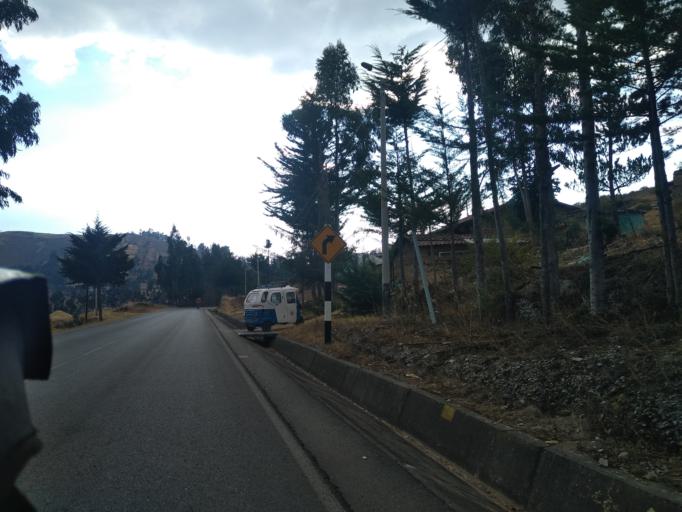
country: PE
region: Cajamarca
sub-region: Provincia de Cajamarca
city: Llacanora
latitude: -7.1434
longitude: -78.4039
